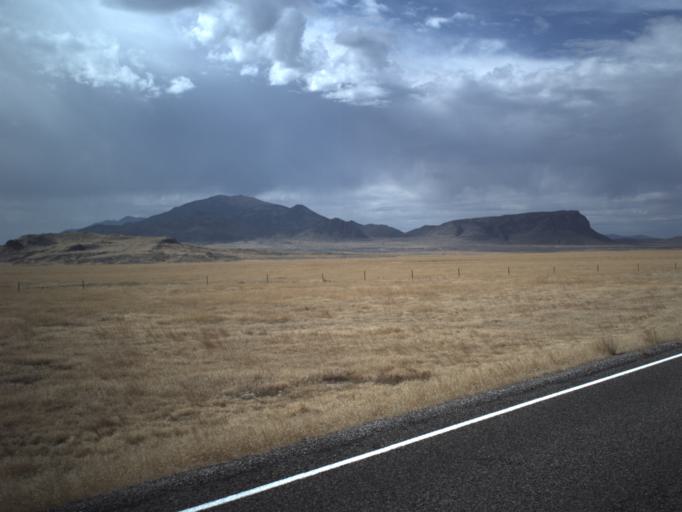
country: US
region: Utah
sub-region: Tooele County
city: Wendover
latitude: 41.3929
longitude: -113.9680
